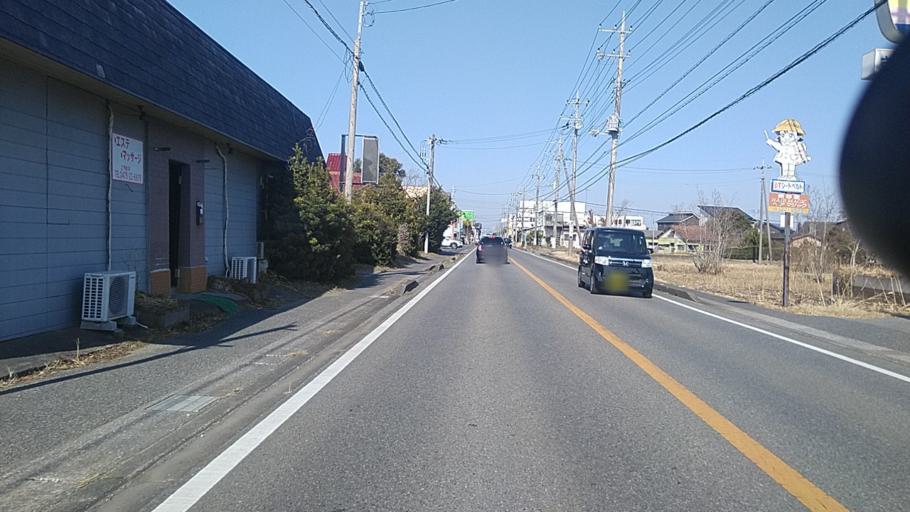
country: JP
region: Chiba
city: Mobara
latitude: 35.4426
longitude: 140.2952
